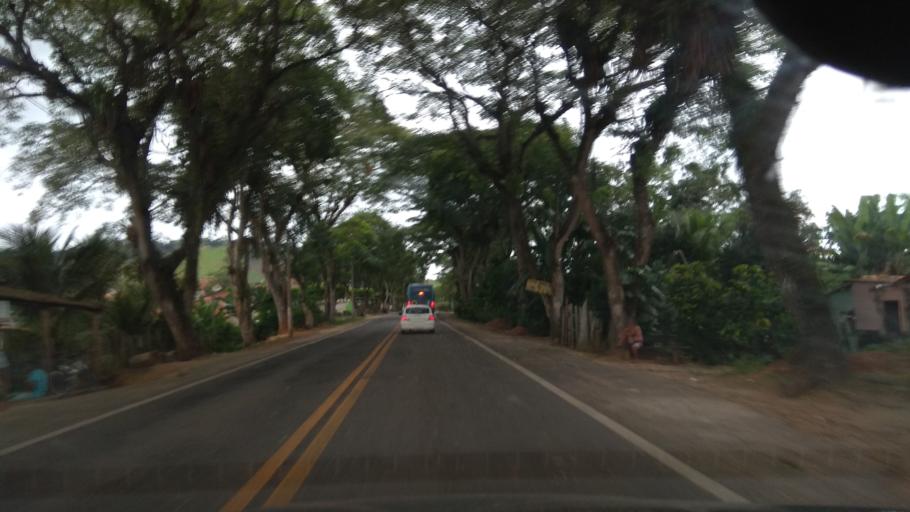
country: BR
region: Bahia
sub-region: Ubata
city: Ubata
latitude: -14.1987
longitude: -39.5376
